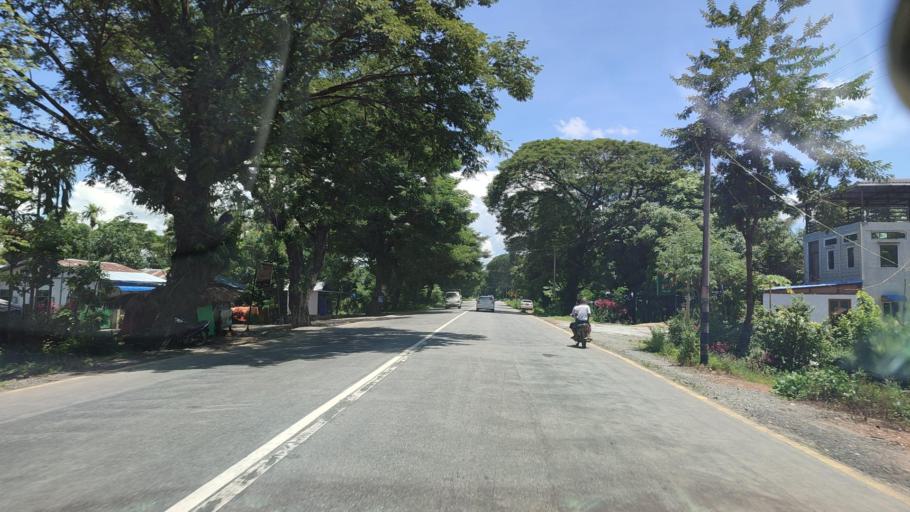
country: MM
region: Bago
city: Pyu
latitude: 18.2504
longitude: 96.5339
